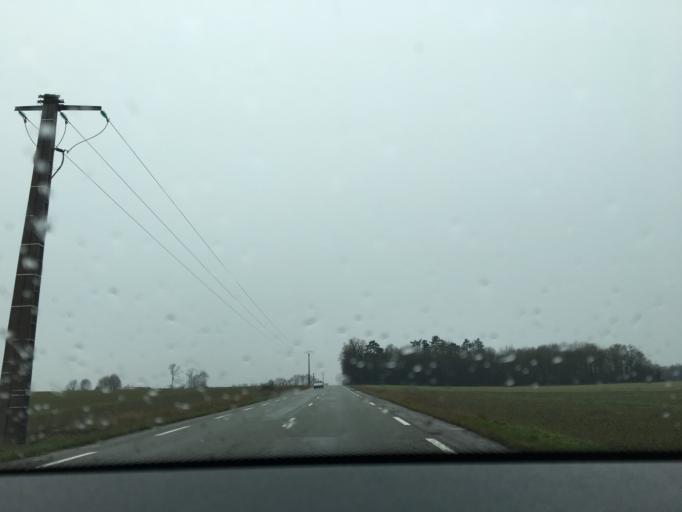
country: FR
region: Ile-de-France
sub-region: Departement des Yvelines
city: Limay
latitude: 49.0245
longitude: 1.7429
